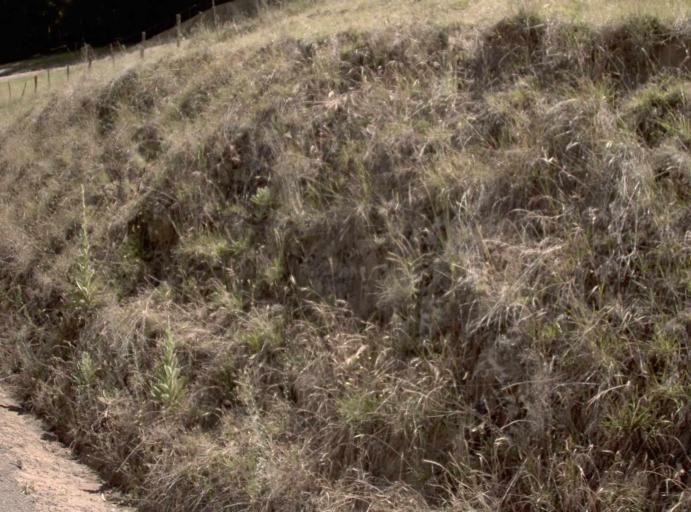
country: AU
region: New South Wales
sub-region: Bombala
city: Bombala
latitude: -37.1241
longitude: 148.6631
